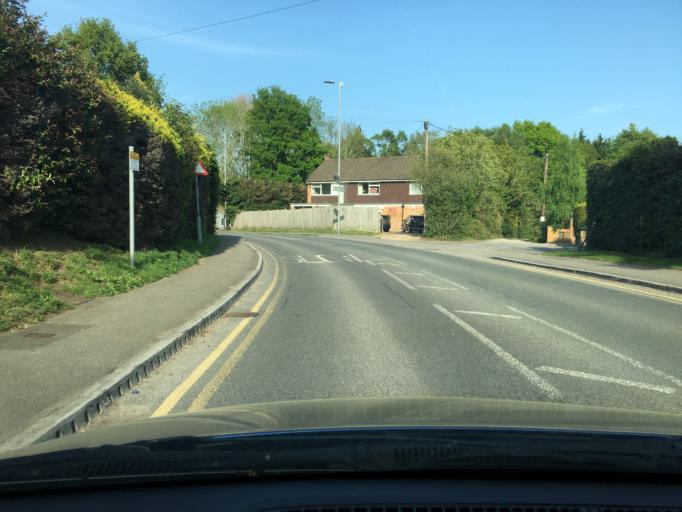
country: GB
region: England
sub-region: Bracknell Forest
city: Sandhurst
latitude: 51.3467
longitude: -0.8057
